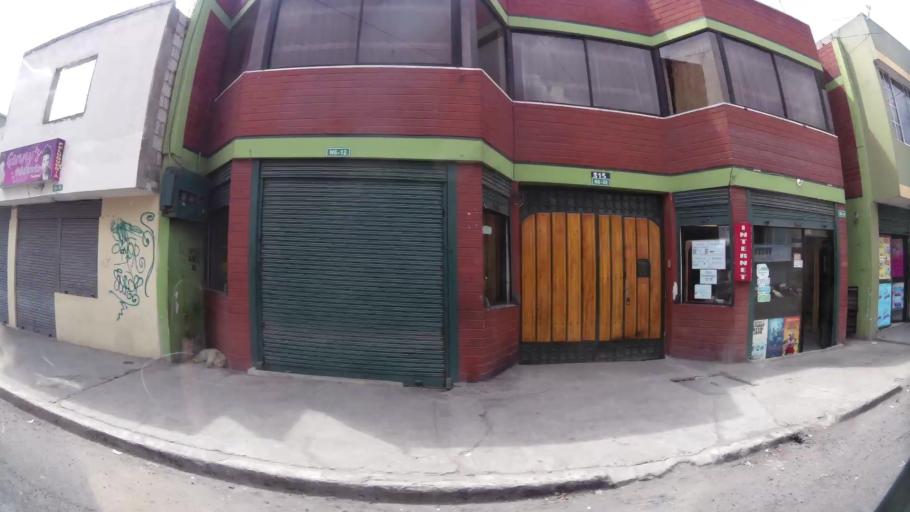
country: EC
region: Pichincha
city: Quito
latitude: -0.0801
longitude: -78.4134
